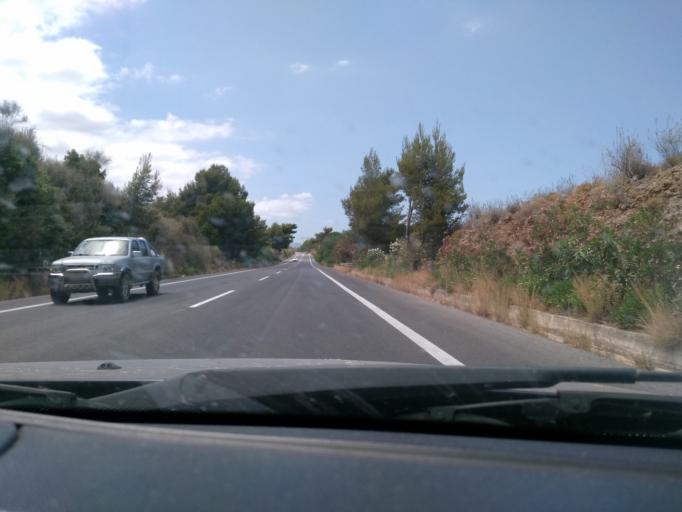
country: GR
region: Crete
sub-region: Nomos Chanias
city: Georgioupolis
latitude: 35.3644
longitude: 24.2371
